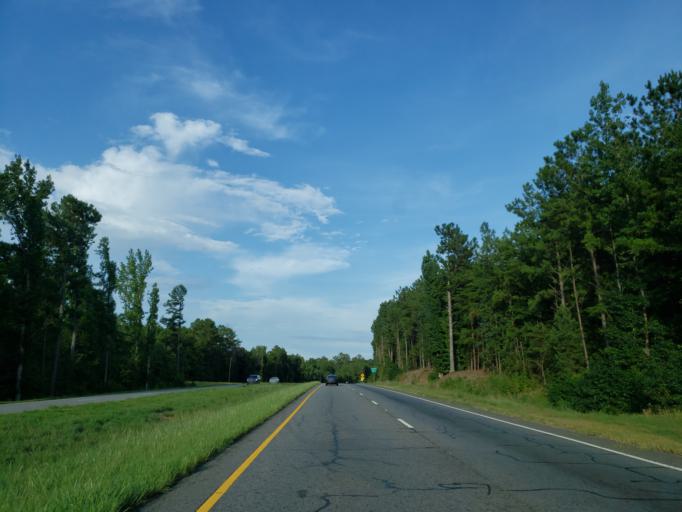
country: US
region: Georgia
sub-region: Bartow County
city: Euharlee
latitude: 34.2106
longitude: -84.9726
